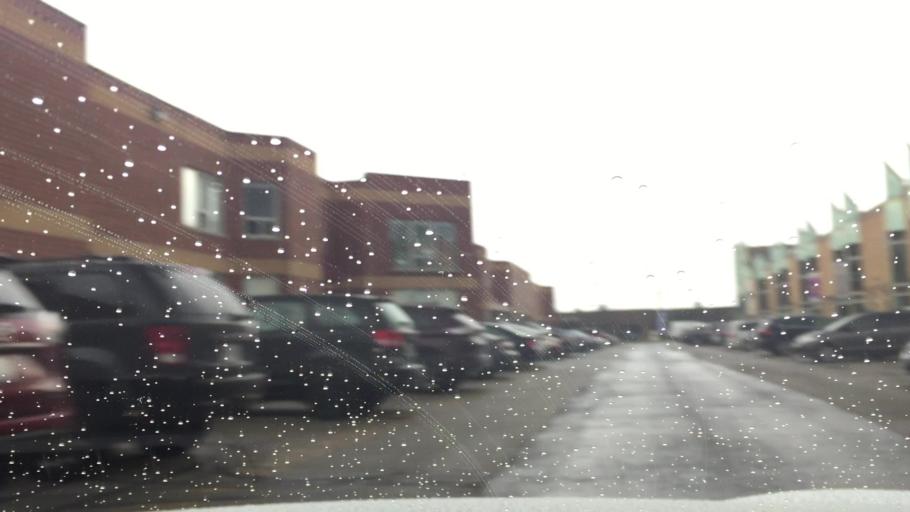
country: CA
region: Ontario
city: Mississauga
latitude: 43.6265
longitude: -79.6338
